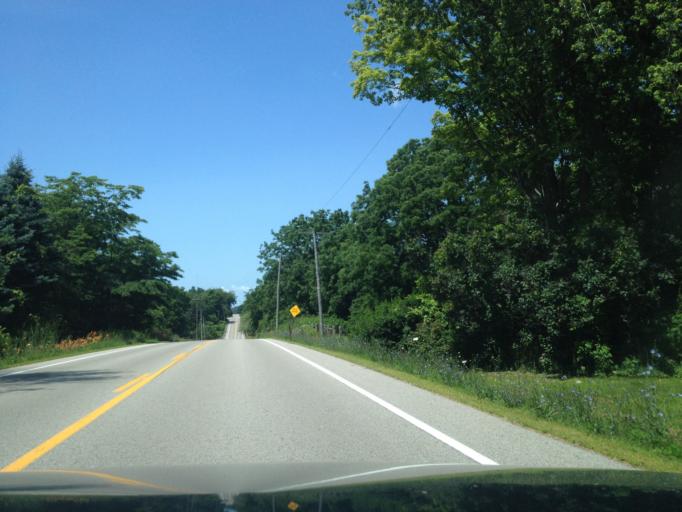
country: CA
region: Ontario
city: Norfolk County
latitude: 42.5815
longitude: -80.5860
